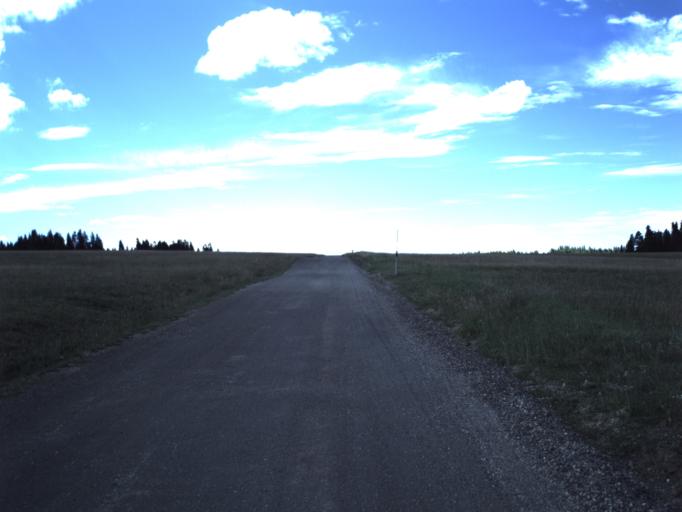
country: US
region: Utah
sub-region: Piute County
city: Junction
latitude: 38.2808
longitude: -112.3608
